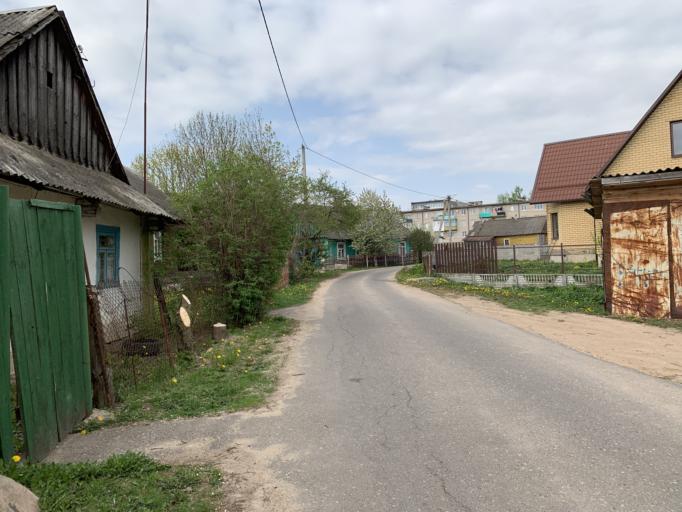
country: BY
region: Minsk
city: Nyasvizh
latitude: 53.2169
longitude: 26.6782
